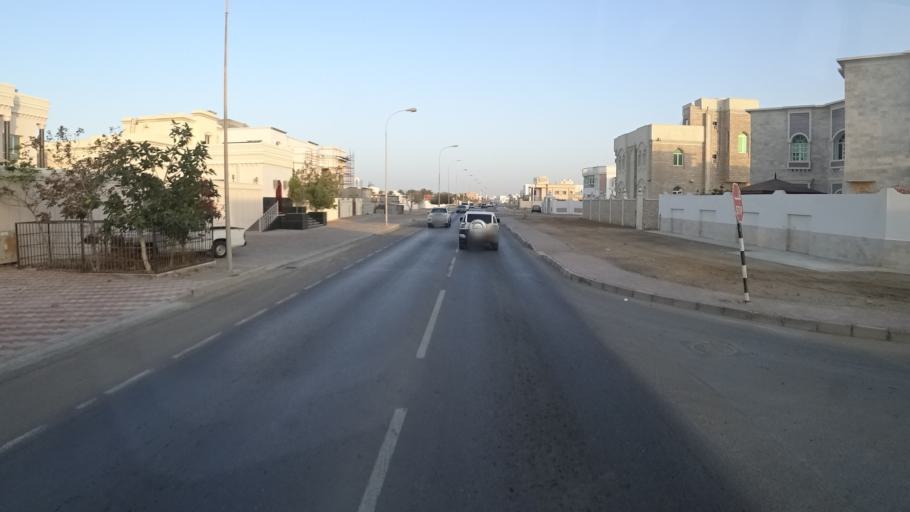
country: OM
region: Ash Sharqiyah
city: Sur
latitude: 22.5924
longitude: 59.4989
